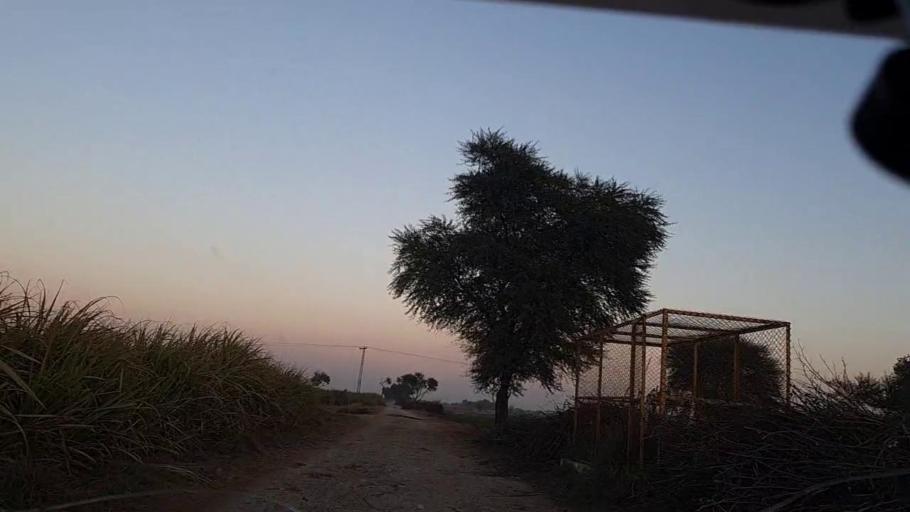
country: PK
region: Sindh
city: Adilpur
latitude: 27.8544
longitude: 69.2908
